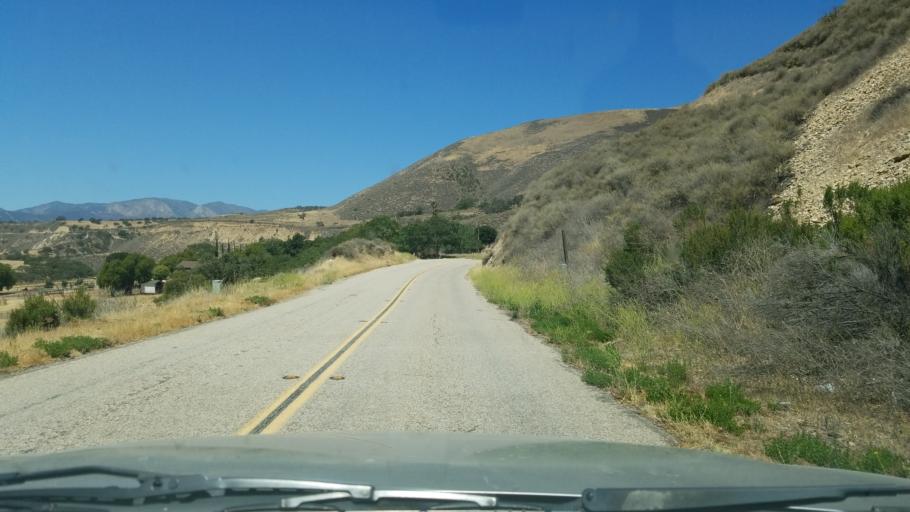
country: US
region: California
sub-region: Monterey County
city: Greenfield
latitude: 36.2704
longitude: -121.3387
